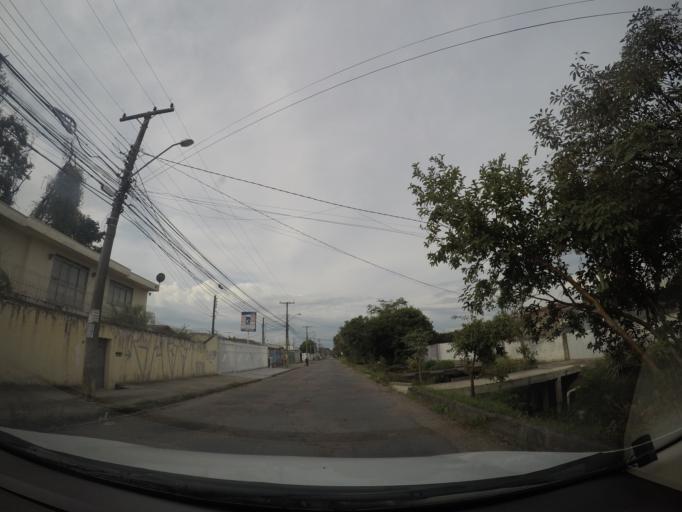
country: BR
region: Parana
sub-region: Sao Jose Dos Pinhais
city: Sao Jose dos Pinhais
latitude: -25.5020
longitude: -49.2342
